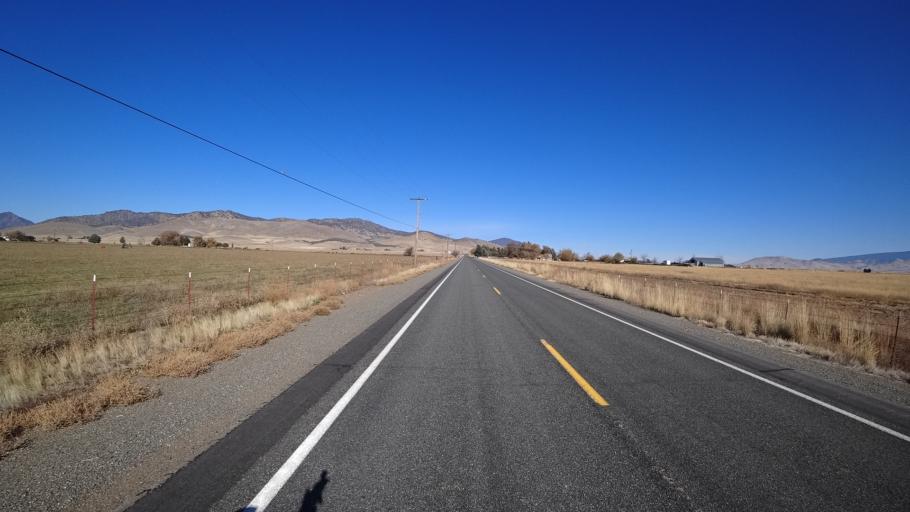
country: US
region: California
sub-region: Siskiyou County
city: Montague
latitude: 41.7611
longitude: -122.5247
